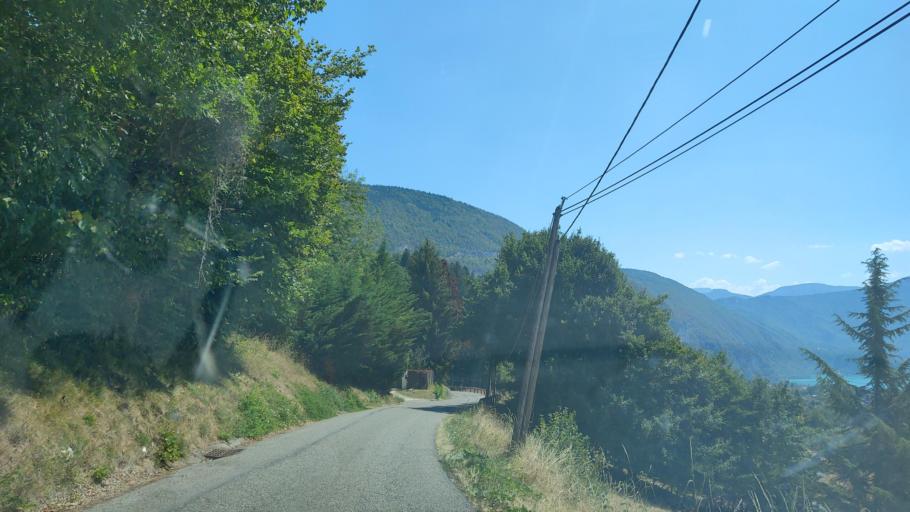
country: FR
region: Rhone-Alpes
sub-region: Departement de la Savoie
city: Novalaise
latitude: 45.6067
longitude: 5.7834
